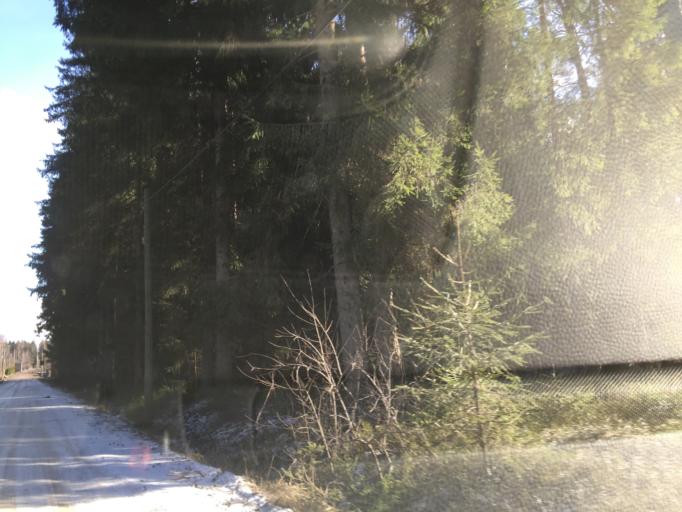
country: LV
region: Garkalne
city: Garkalne
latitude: 56.9508
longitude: 24.4468
